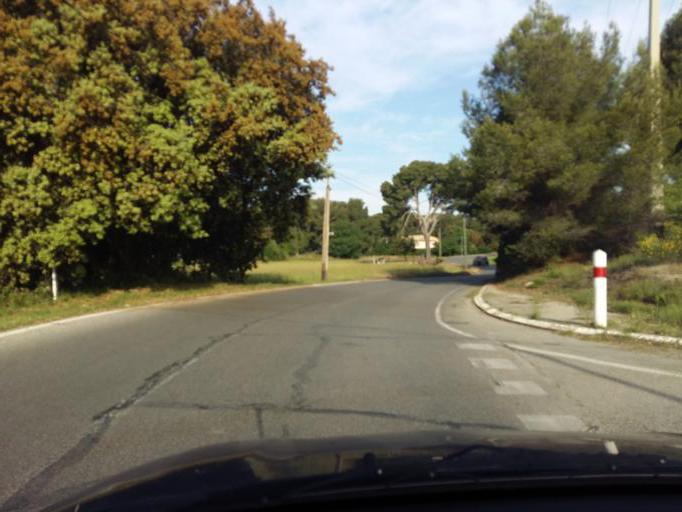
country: FR
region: Provence-Alpes-Cote d'Azur
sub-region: Departement des Bouches-du-Rhone
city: Pelissanne
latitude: 43.6358
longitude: 5.1253
